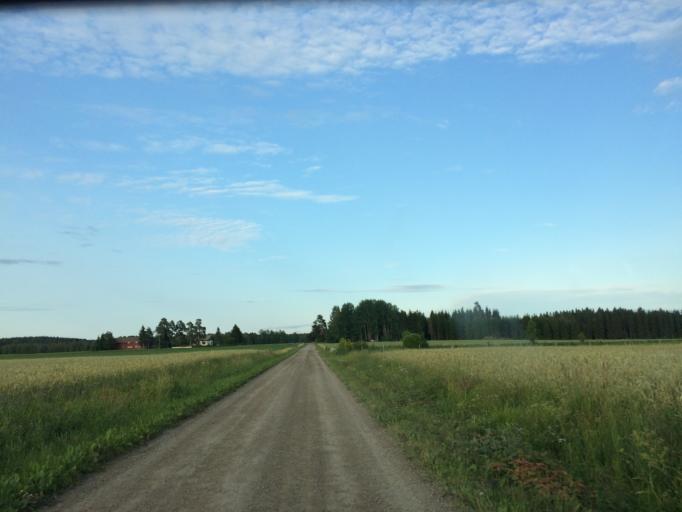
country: FI
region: Haeme
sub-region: Haemeenlinna
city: Janakkala
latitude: 60.8778
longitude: 24.6296
